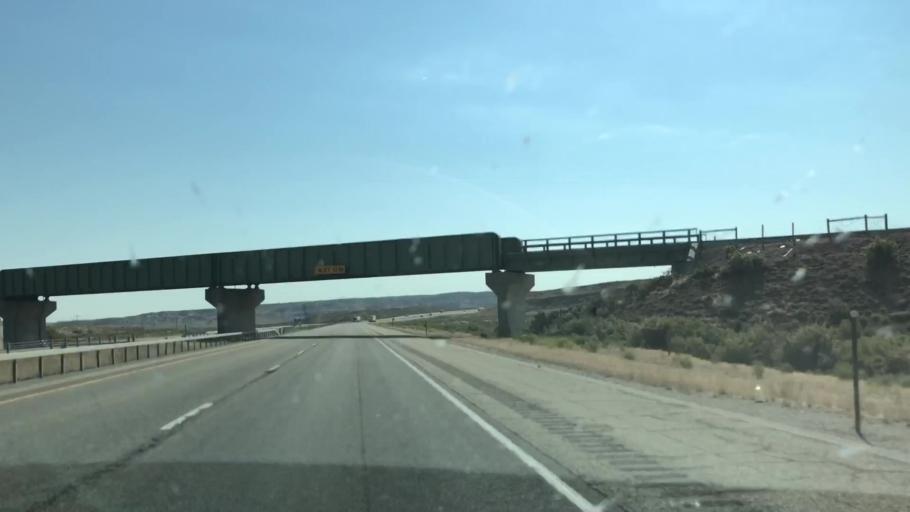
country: US
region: Wyoming
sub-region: Sweetwater County
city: Rock Springs
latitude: 41.6740
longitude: -108.7487
